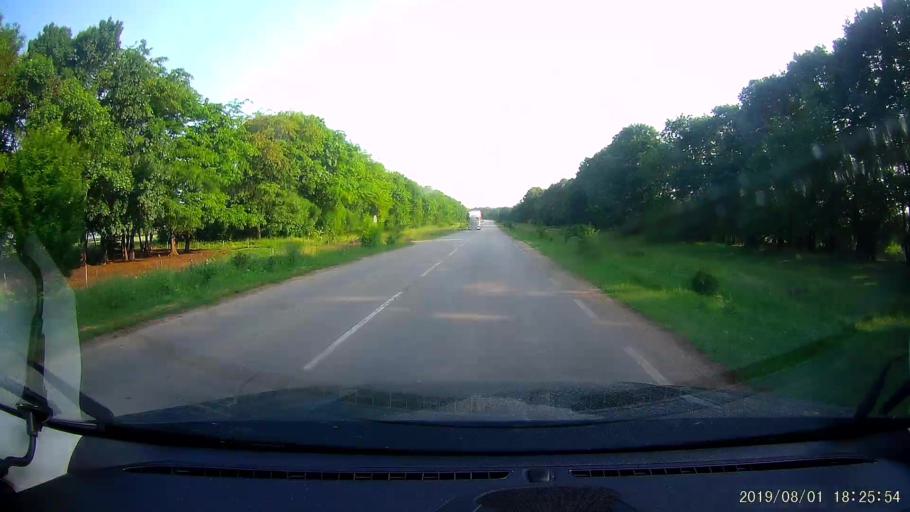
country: BG
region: Shumen
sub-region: Obshtina Venets
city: Venets
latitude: 43.6108
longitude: 26.9951
